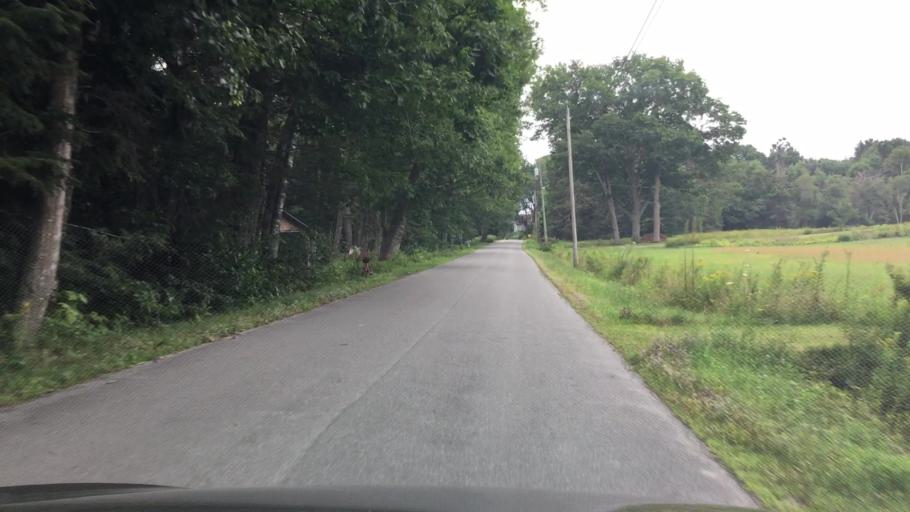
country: US
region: Maine
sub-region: Waldo County
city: Stockton Springs
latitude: 44.5109
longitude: -68.8106
